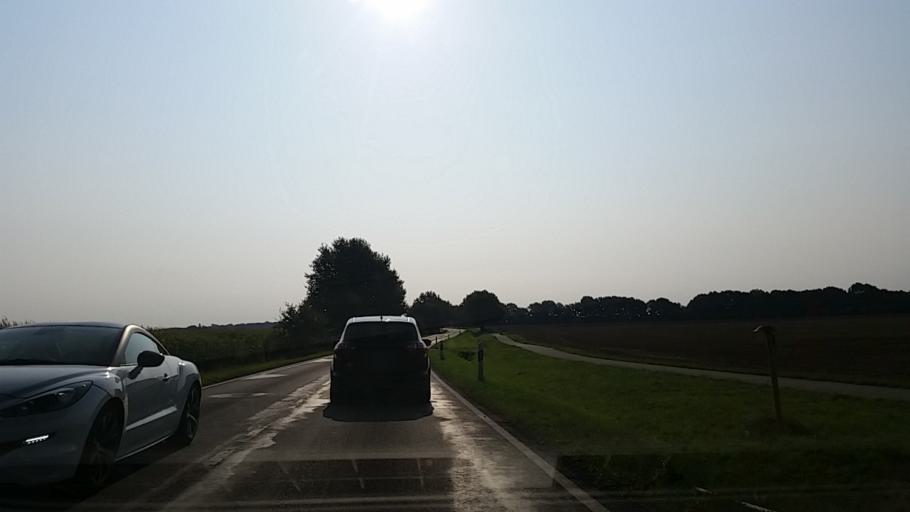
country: DE
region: Mecklenburg-Vorpommern
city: Wittenburg
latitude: 53.4813
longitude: 11.1213
